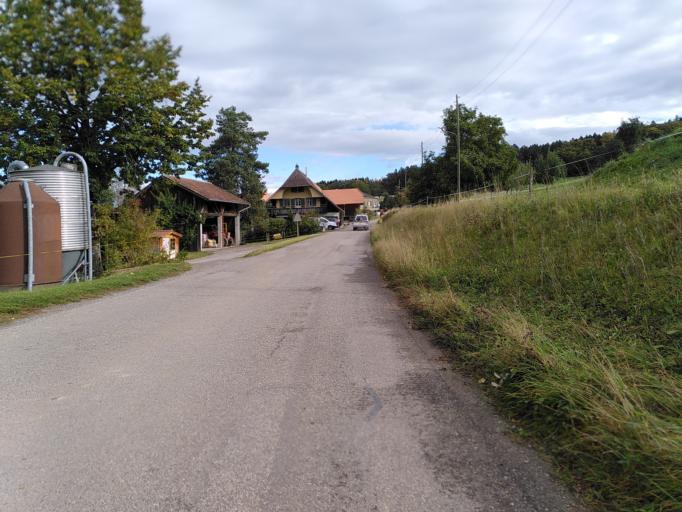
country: CH
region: Bern
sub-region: Emmental District
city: Wynigen
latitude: 47.1033
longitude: 7.6429
